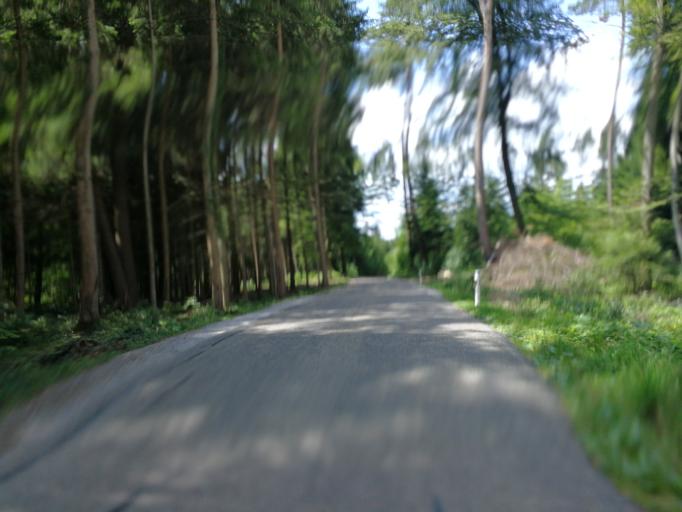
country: CH
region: Zurich
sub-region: Bezirk Hinwil
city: Gruet
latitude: 47.3143
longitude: 8.7717
